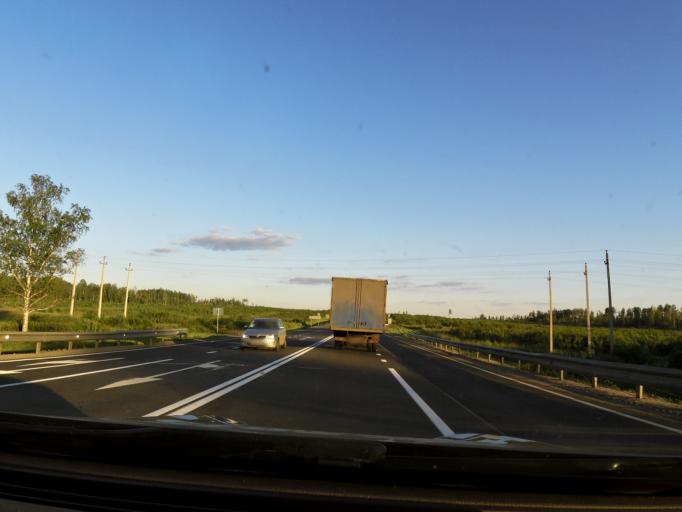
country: RU
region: Jaroslavl
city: Prechistoye
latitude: 58.6324
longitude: 40.3273
